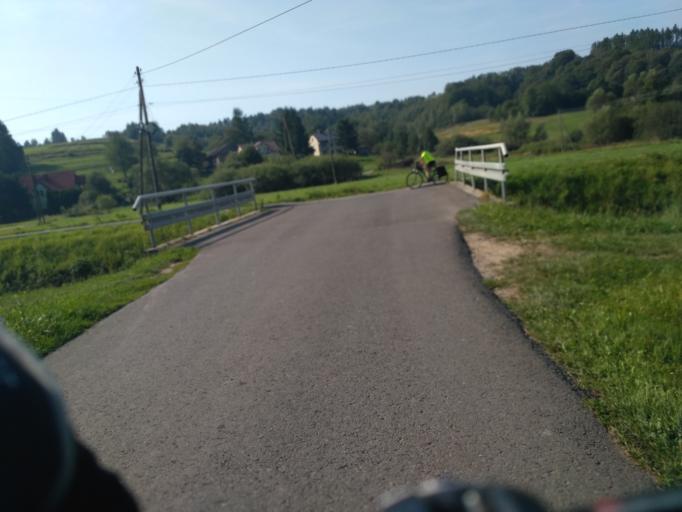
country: PL
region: Subcarpathian Voivodeship
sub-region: Powiat brzozowski
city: Golcowa
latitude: 49.7749
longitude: 22.0152
